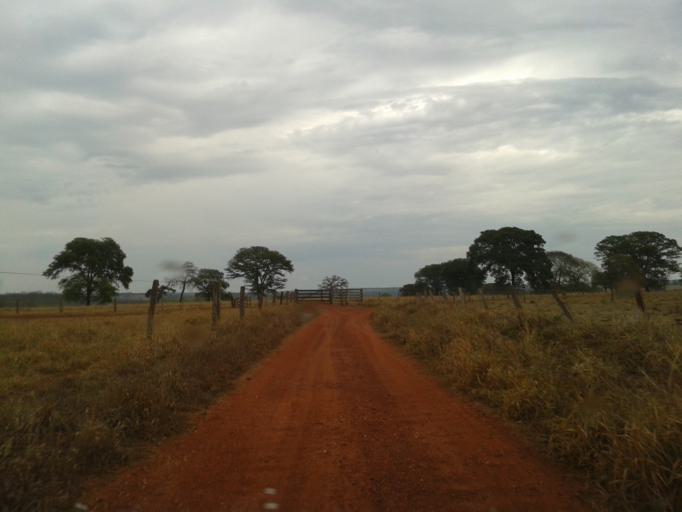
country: BR
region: Minas Gerais
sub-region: Capinopolis
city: Capinopolis
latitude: -18.8718
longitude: -49.8084
